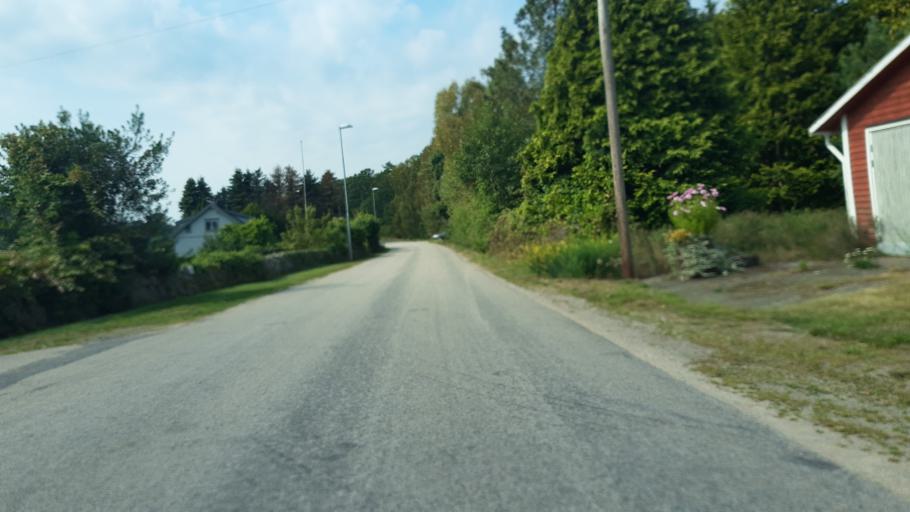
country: SE
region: Blekinge
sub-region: Karlskrona Kommun
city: Nattraby
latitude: 56.1763
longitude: 15.4856
